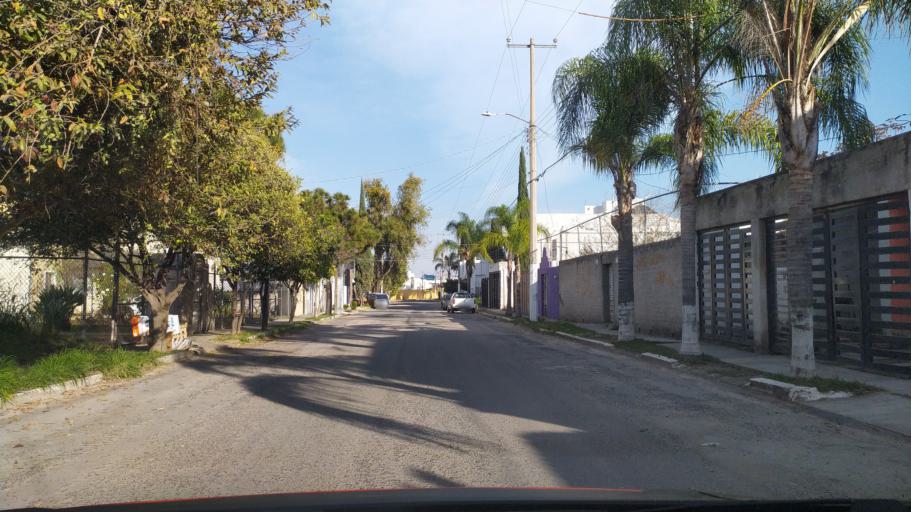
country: MX
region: Jalisco
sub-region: Tlajomulco de Zuniga
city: Palomar
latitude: 20.6267
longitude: -103.4714
